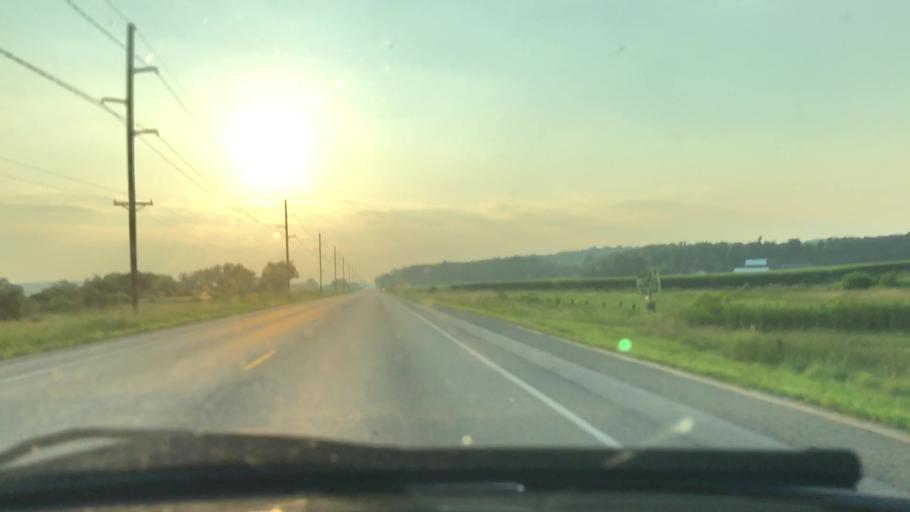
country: US
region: Wisconsin
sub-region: Dane County
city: Black Earth
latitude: 43.1245
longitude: -89.7035
